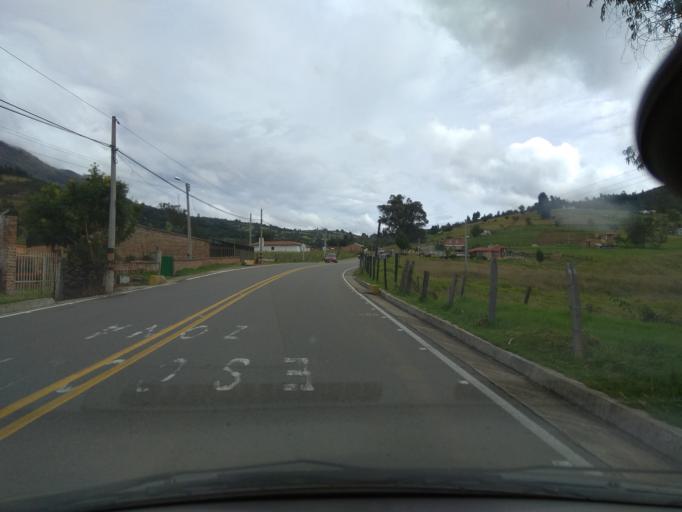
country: CO
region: Boyaca
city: Santa Rosa de Viterbo
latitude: 5.8856
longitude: -72.9798
